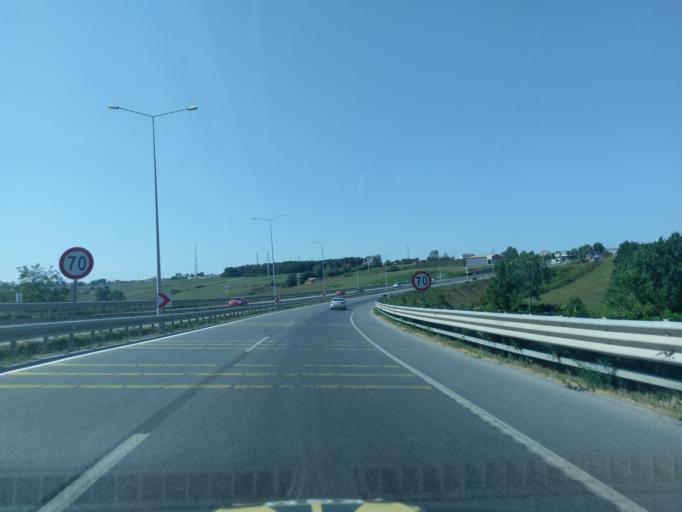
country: TR
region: Samsun
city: Bafra
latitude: 41.5414
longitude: 35.9331
